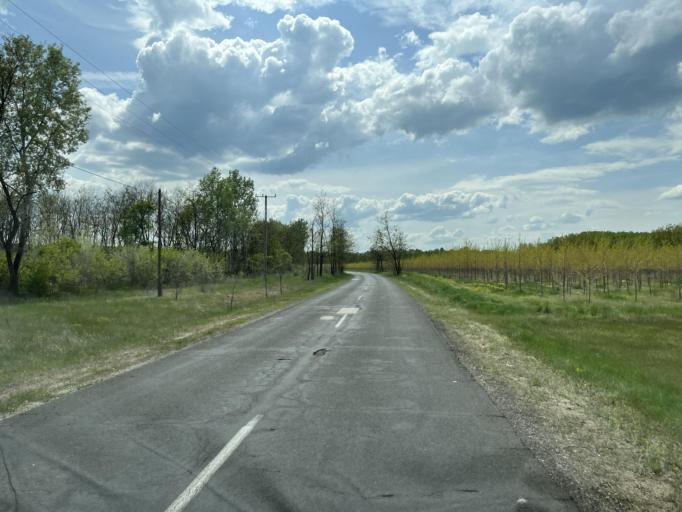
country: HU
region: Pest
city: Csemo
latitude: 47.1253
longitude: 19.6550
